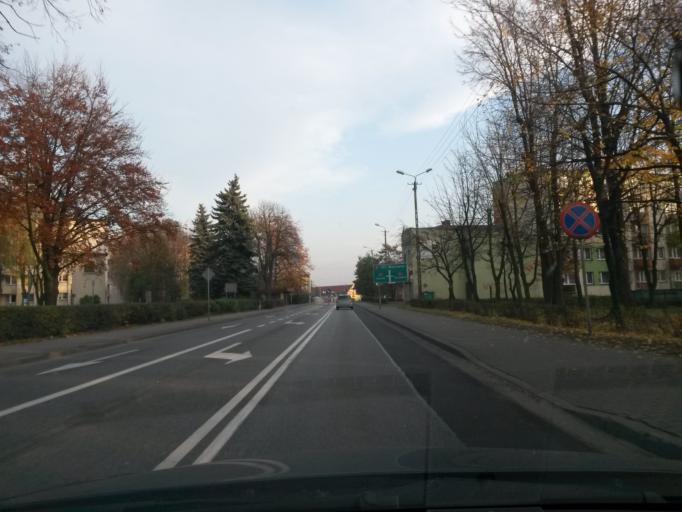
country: PL
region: Lodz Voivodeship
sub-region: Powiat wielunski
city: Wielun
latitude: 51.2264
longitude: 18.5587
